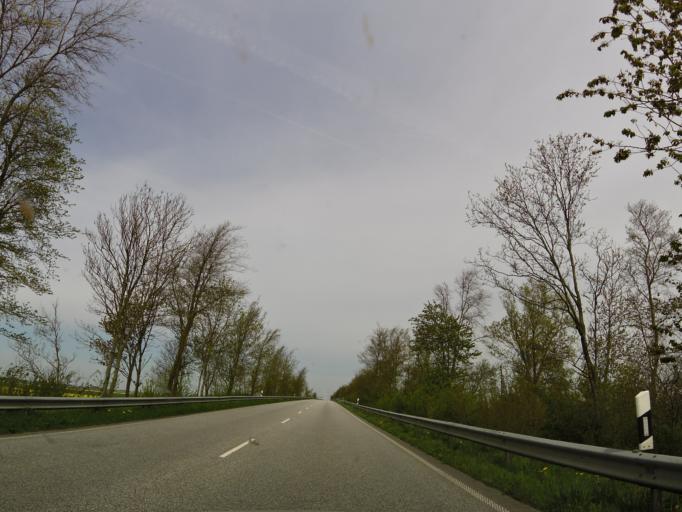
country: DE
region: Schleswig-Holstein
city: Lohe-Rickelshof
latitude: 54.2177
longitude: 9.0445
